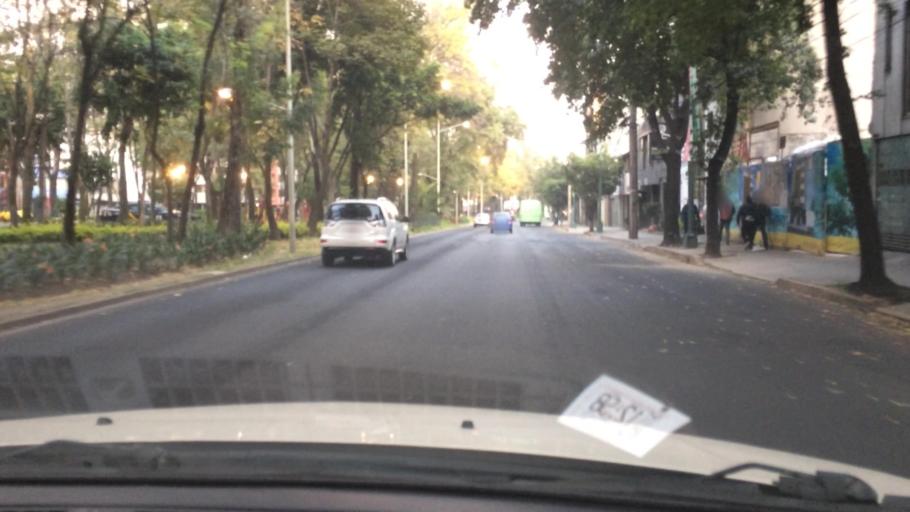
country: MX
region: Mexico City
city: Alvaro Obregon
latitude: 19.3635
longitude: -99.1949
